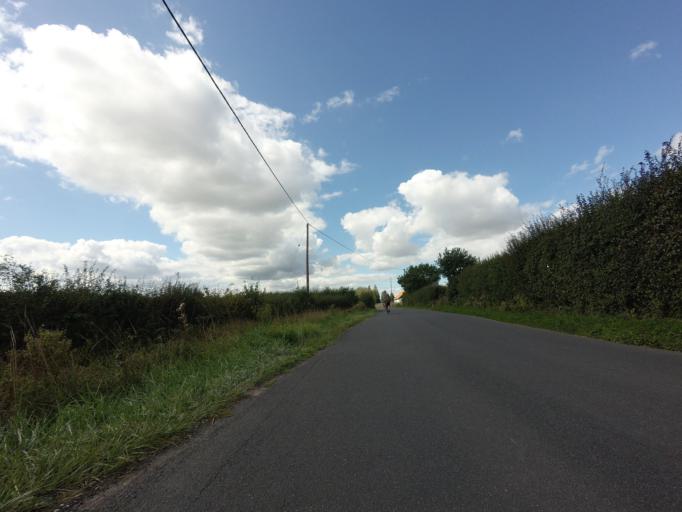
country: GB
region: England
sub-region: Kent
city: Staplehurst
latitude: 51.1521
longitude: 0.5395
